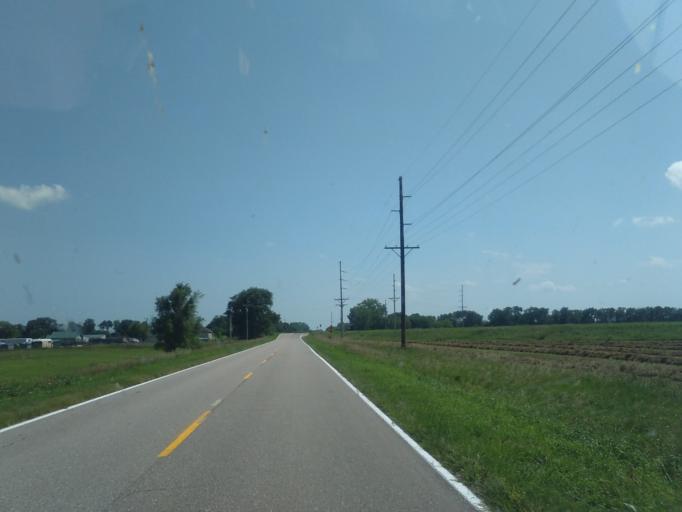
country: US
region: Nebraska
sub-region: Phelps County
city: Holdrege
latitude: 40.7130
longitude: -99.3794
